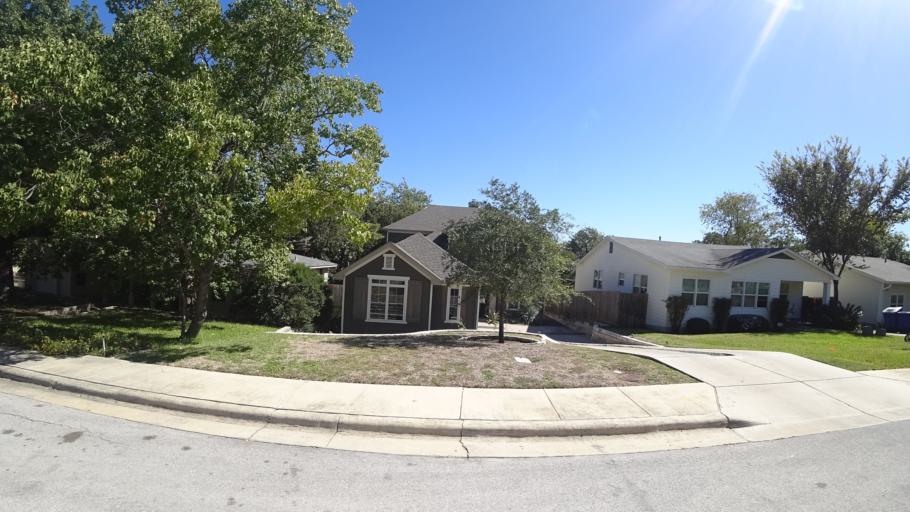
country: US
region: Texas
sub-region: Travis County
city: Rollingwood
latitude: 30.2947
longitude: -97.7637
